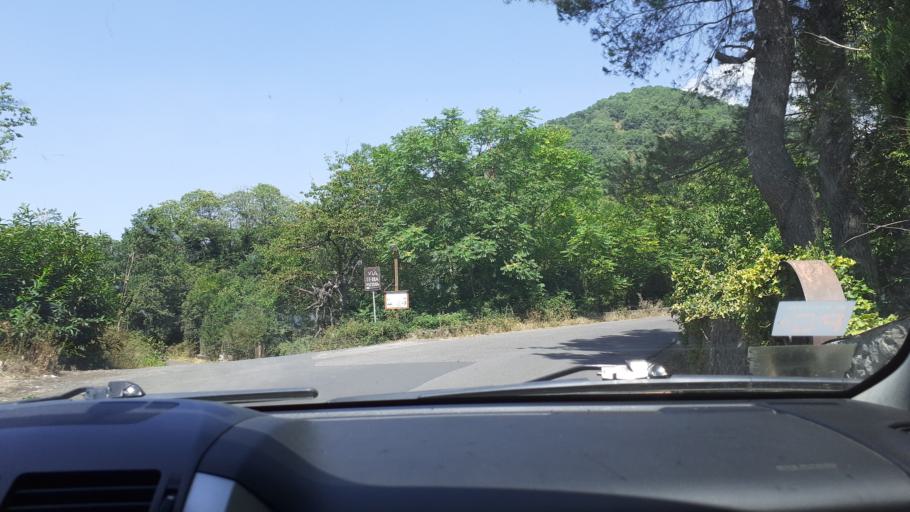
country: IT
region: Sicily
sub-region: Catania
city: Nicolosi
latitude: 37.6372
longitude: 15.0222
